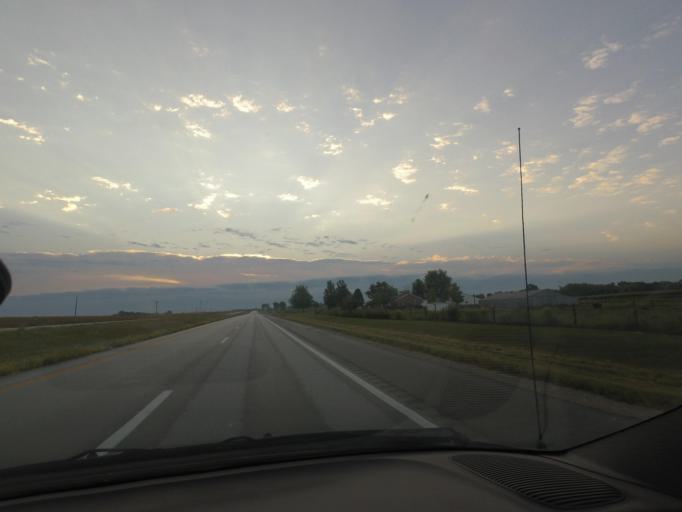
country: US
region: Missouri
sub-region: Macon County
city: Macon
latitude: 39.7501
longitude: -92.2852
